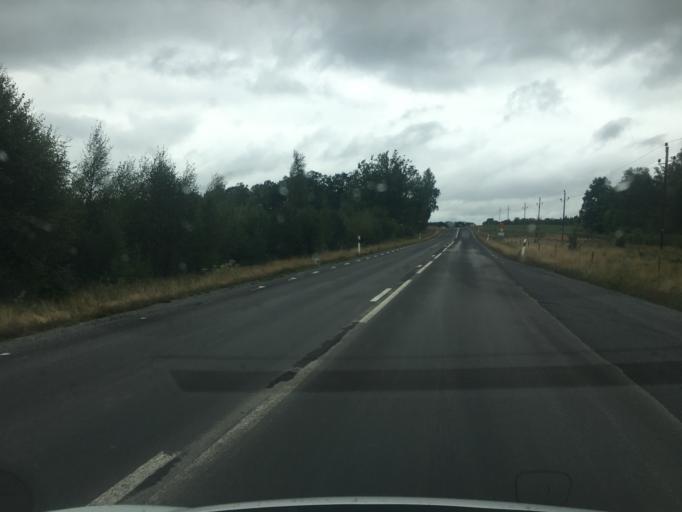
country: SE
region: Kronoberg
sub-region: Ljungby Kommun
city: Lagan
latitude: 56.9886
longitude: 14.0107
